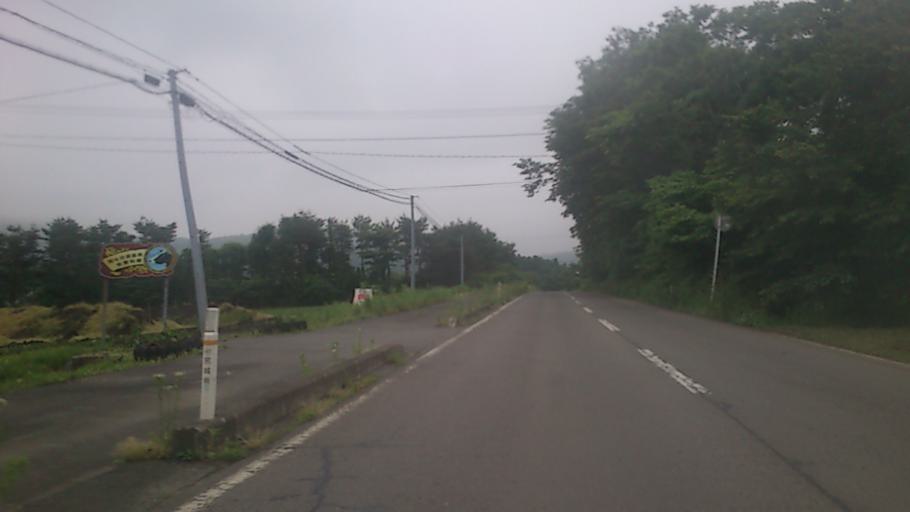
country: JP
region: Miyagi
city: Shiroishi
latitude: 38.1083
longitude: 140.5649
